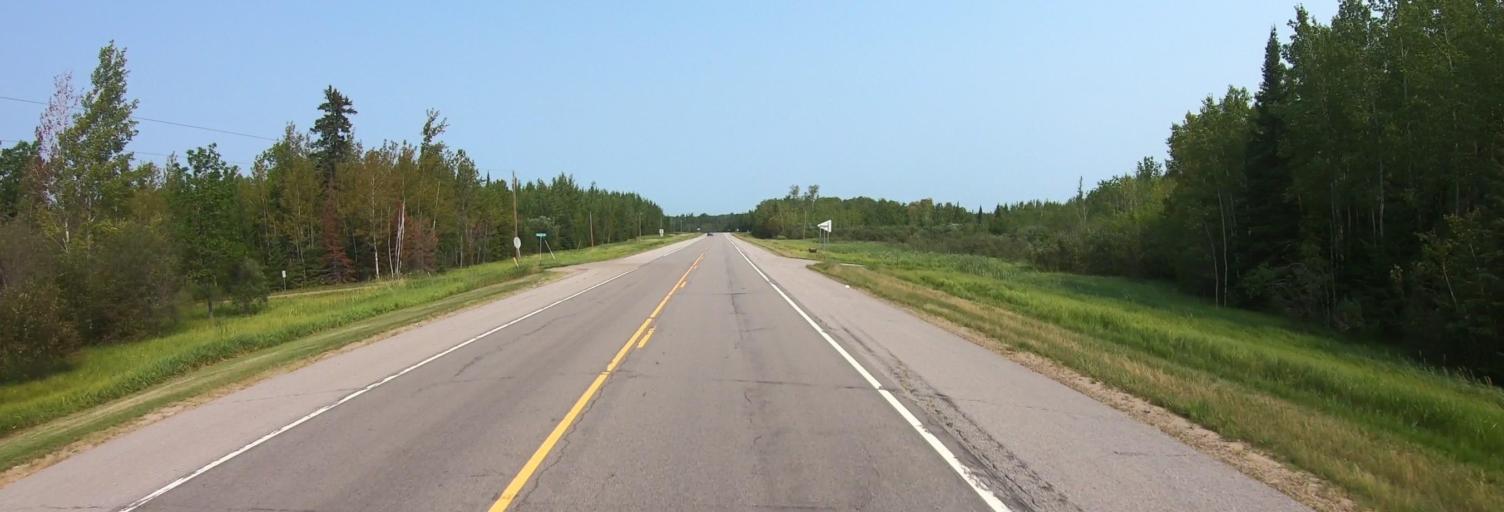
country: US
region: Minnesota
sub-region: Saint Louis County
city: Mountain Iron
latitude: 48.0787
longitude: -92.8221
